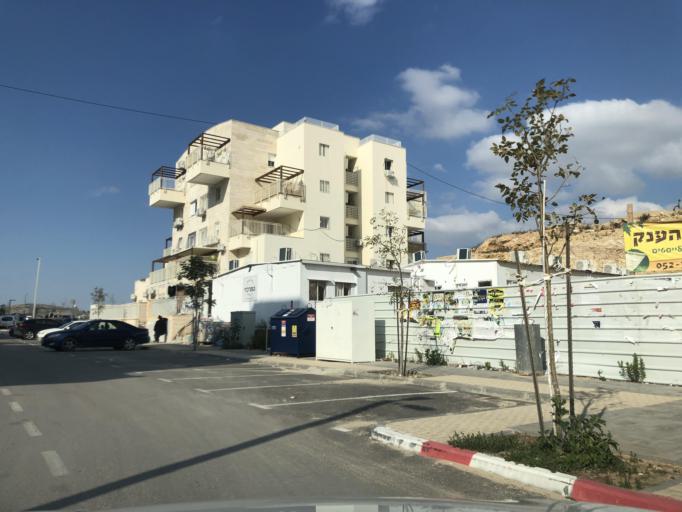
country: IL
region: Jerusalem
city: Modiin Ilit
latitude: 31.9339
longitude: 35.0533
